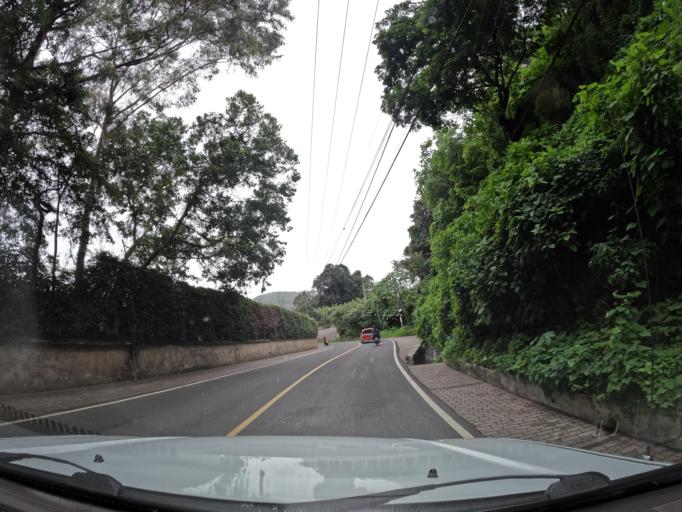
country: GT
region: Sacatepequez
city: Pastores
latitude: 14.5947
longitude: -90.7540
